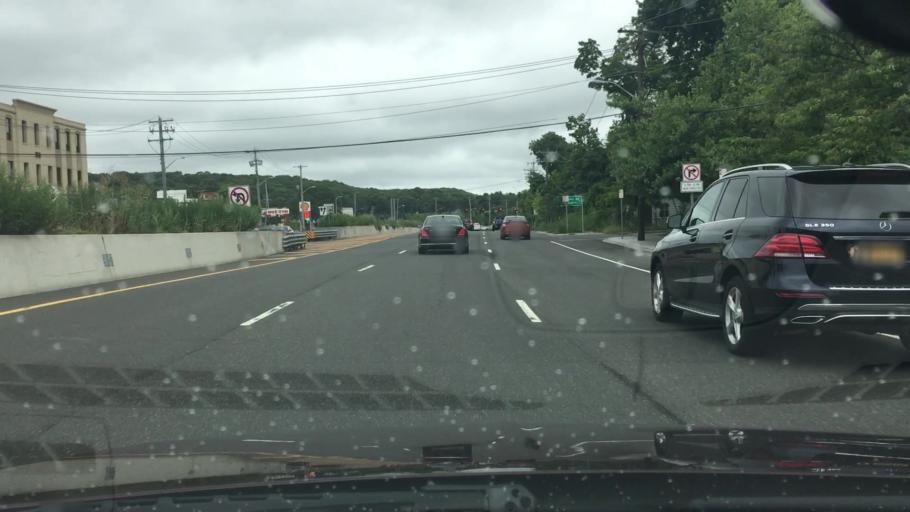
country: US
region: New York
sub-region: Suffolk County
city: Melville
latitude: 40.7916
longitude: -73.4155
